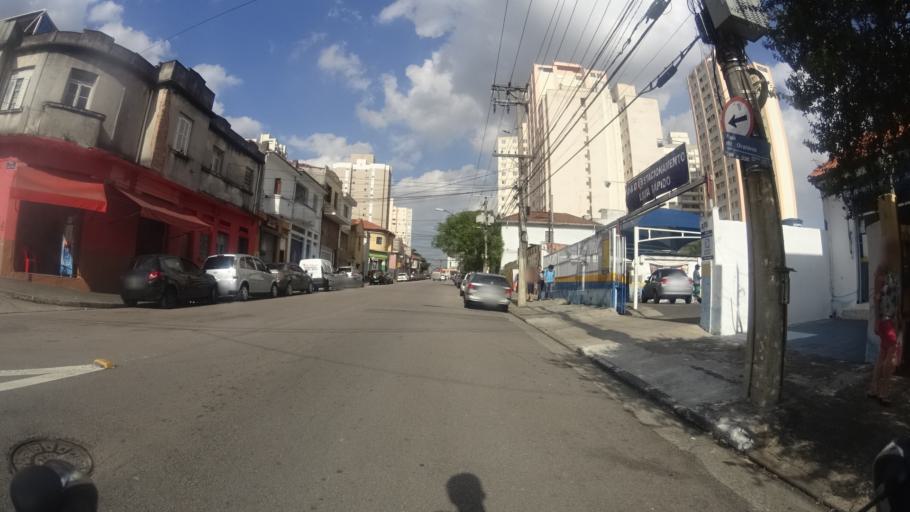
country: BR
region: Sao Paulo
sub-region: Sao Paulo
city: Sao Paulo
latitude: -23.5574
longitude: -46.5972
